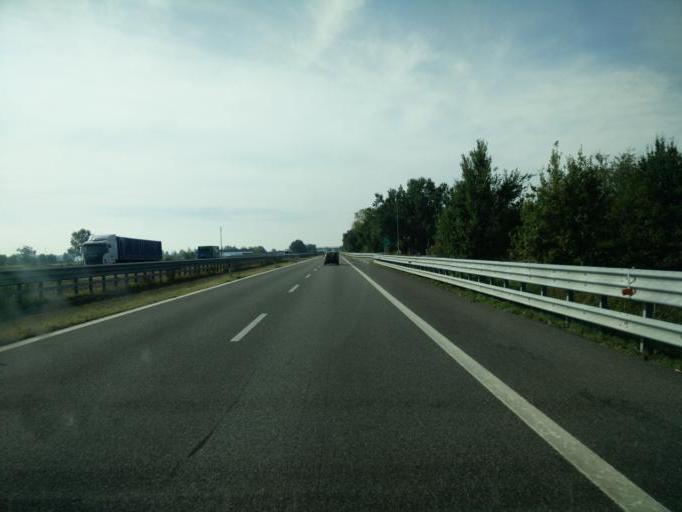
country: IT
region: Lombardy
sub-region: Provincia di Cremona
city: Dosimo
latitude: 45.1719
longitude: 10.0847
